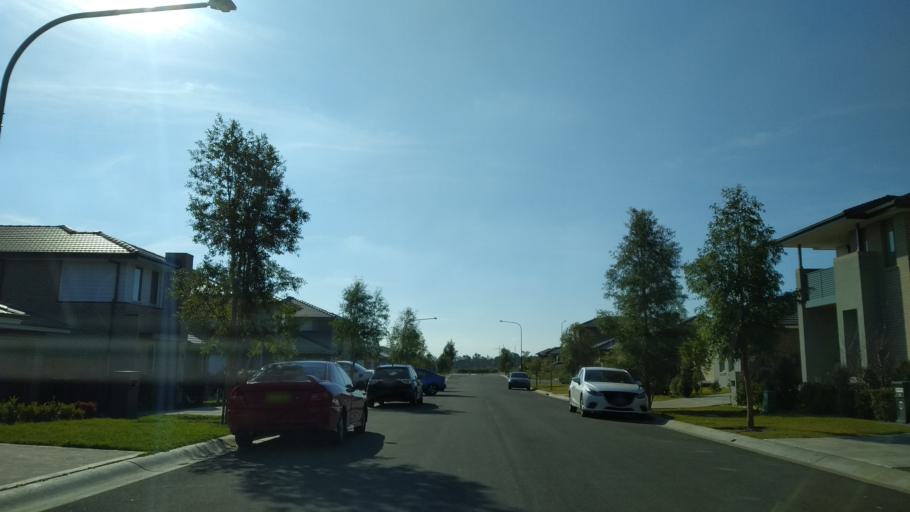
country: AU
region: New South Wales
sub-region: Blacktown
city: Hassall Grove
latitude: -33.7242
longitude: 150.8521
